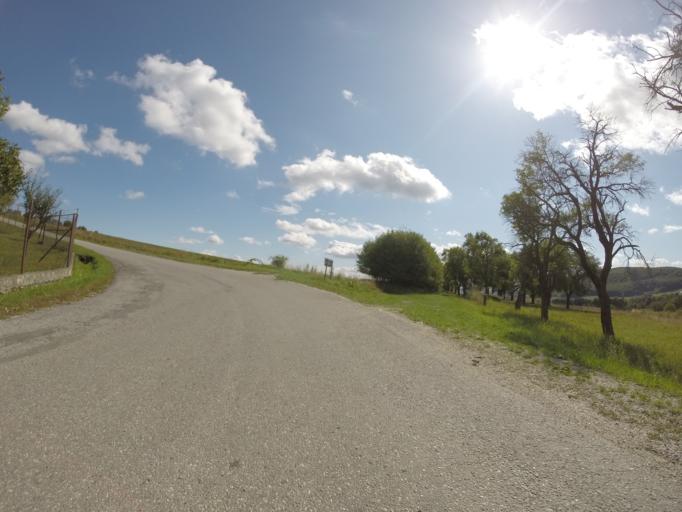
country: SK
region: Nitriansky
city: Stara Tura
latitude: 48.8290
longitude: 17.7286
